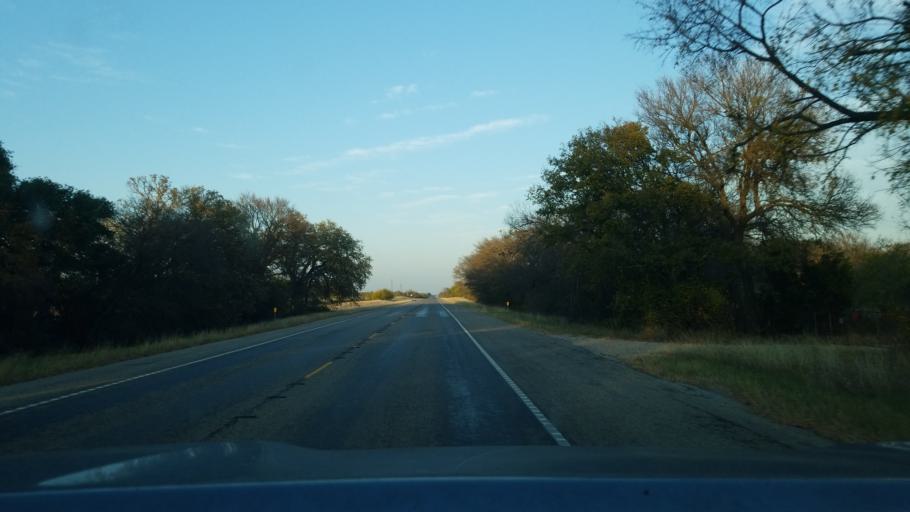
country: US
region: Texas
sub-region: Eastland County
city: Cisco
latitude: 32.4145
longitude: -98.9429
